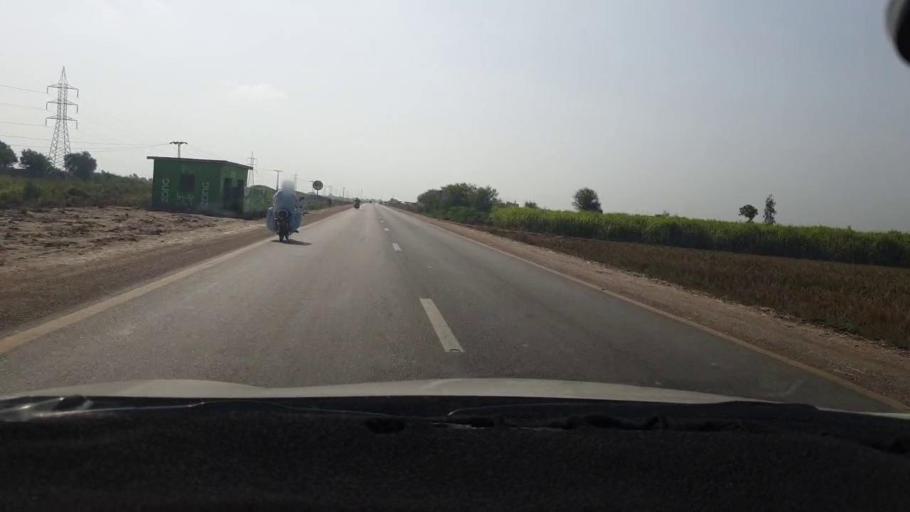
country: PK
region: Sindh
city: Jhol
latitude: 25.9038
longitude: 69.0197
